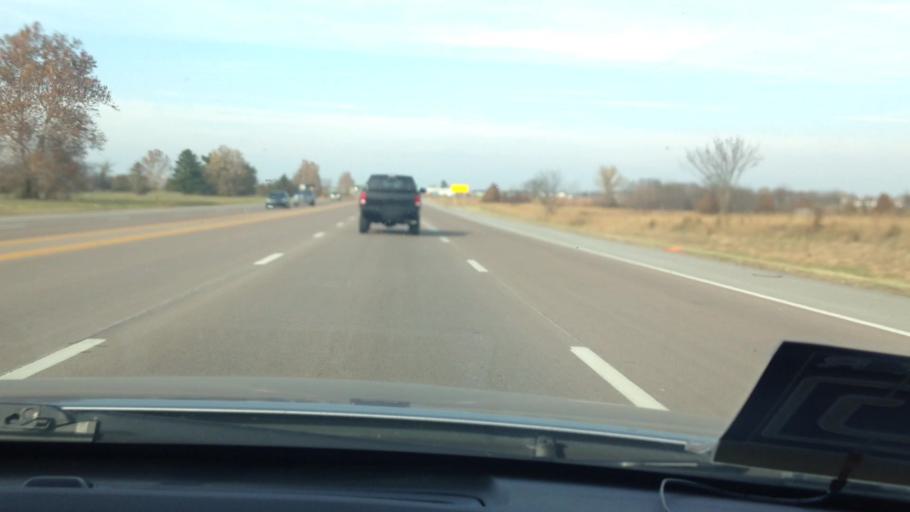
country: US
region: Missouri
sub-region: Henry County
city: Clinton
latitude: 38.3743
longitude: -93.7518
